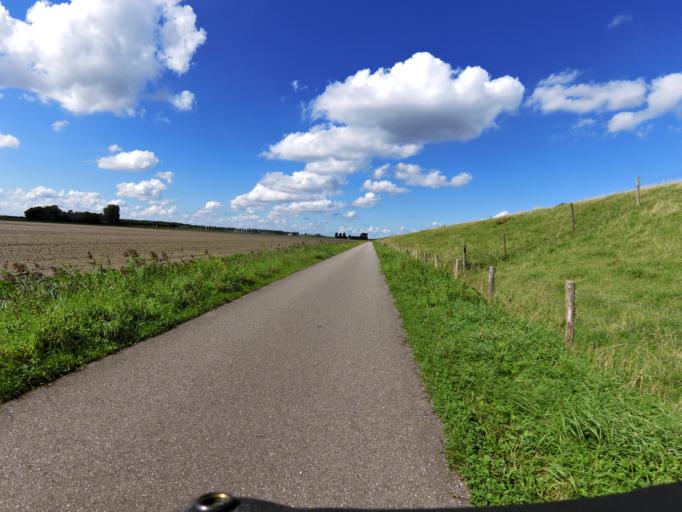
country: NL
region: North Brabant
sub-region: Gemeente Steenbergen
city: Dinteloord
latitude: 51.7105
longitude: 4.3077
